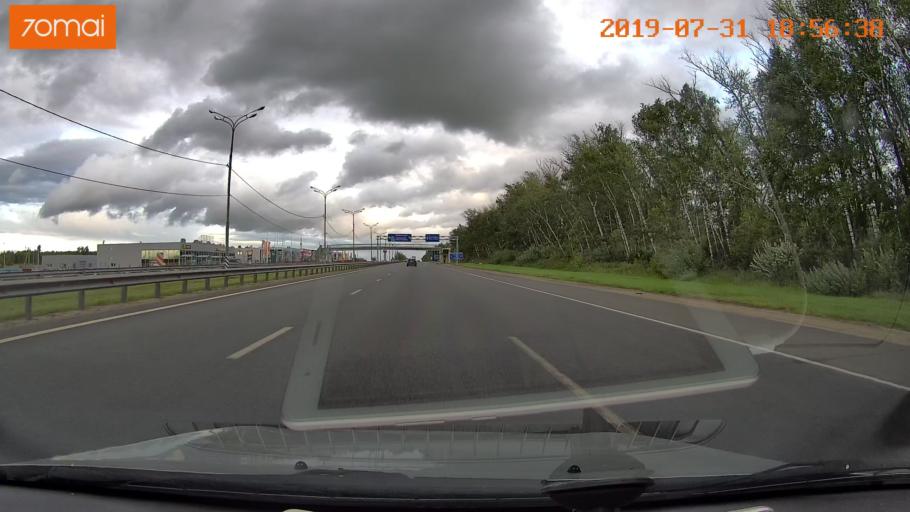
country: RU
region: Moskovskaya
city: Raduzhnyy
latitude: 55.1612
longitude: 38.6808
